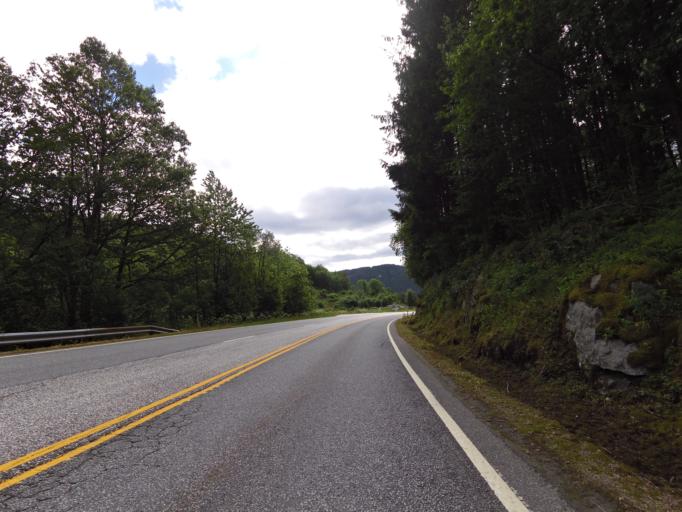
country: NO
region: Vest-Agder
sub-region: Flekkefjord
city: Flekkefjord
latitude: 58.2662
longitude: 6.8066
